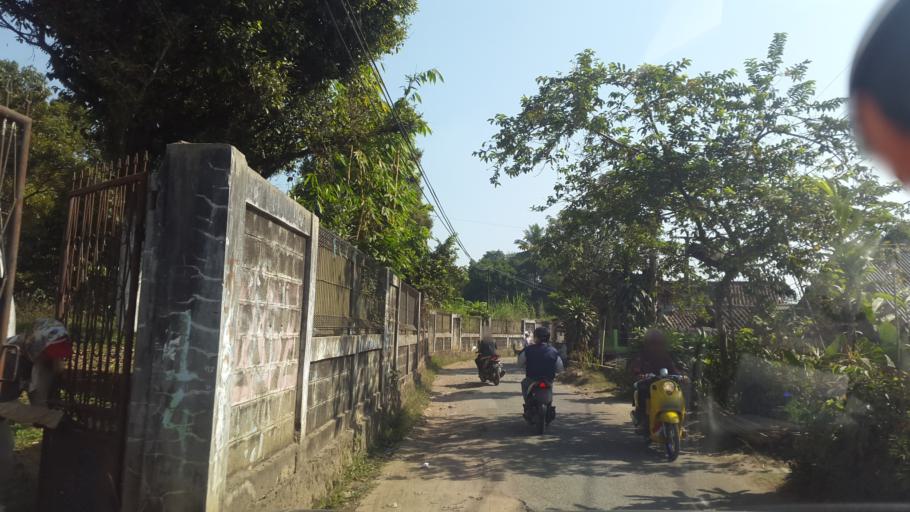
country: ID
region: West Java
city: Cicurug
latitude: -6.8586
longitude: 106.8023
